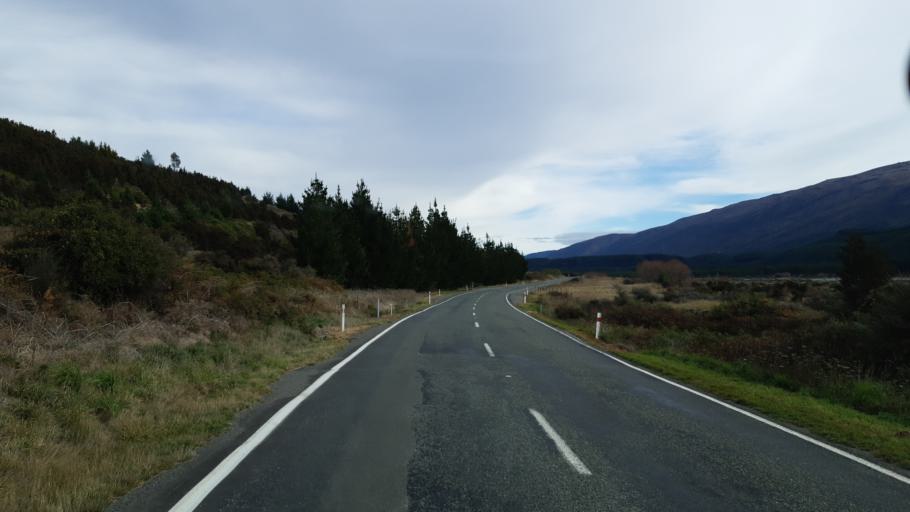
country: NZ
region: Tasman
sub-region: Tasman District
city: Wakefield
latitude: -41.6911
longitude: 173.1501
